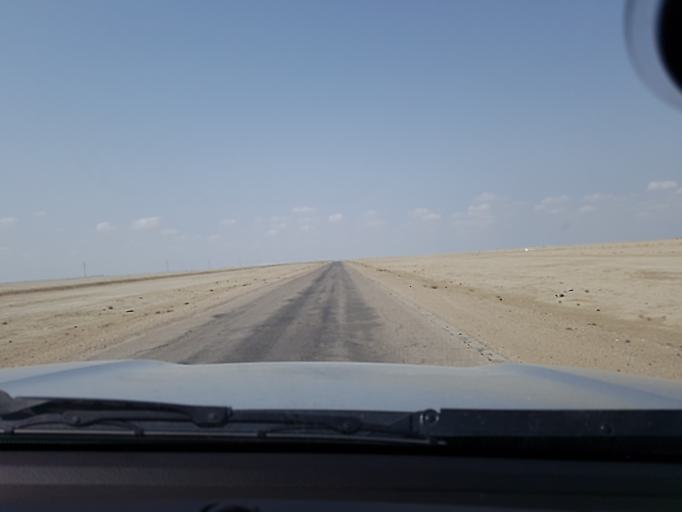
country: TM
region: Balkan
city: Gumdag
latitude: 38.6588
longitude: 54.3935
